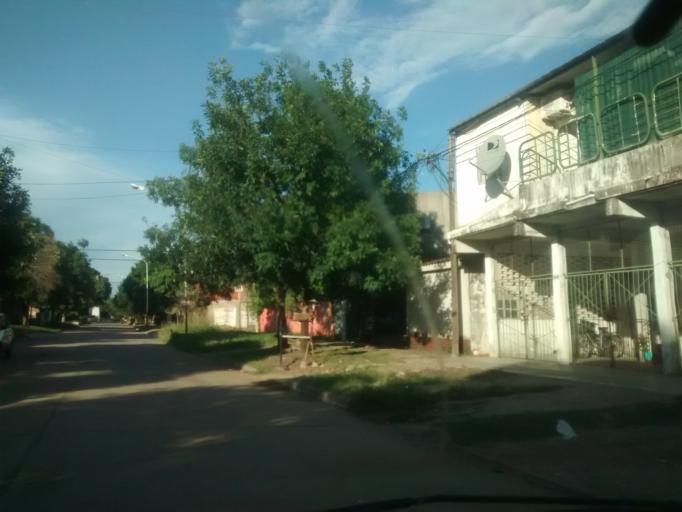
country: AR
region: Chaco
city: Resistencia
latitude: -27.4411
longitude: -59.0057
